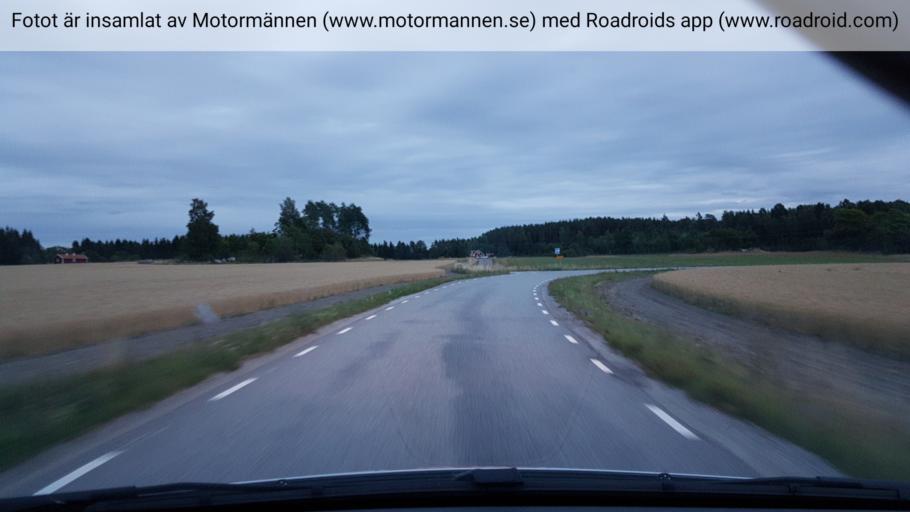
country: SE
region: Vaestmanland
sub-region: Vasteras
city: Tillberga
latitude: 59.5706
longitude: 16.7402
